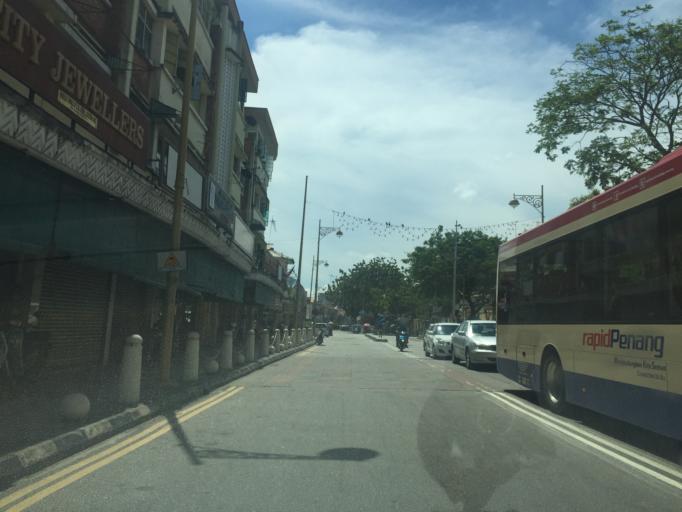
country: MY
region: Penang
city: George Town
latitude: 5.4167
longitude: 100.3378
